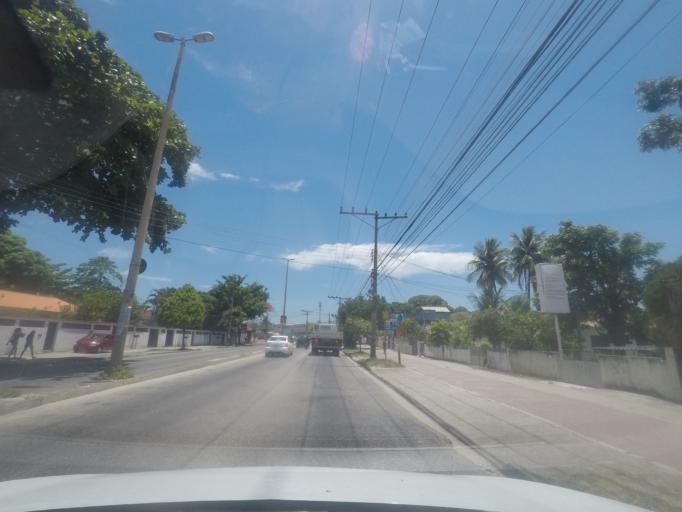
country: BR
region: Rio de Janeiro
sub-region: Itaguai
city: Itaguai
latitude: -22.9095
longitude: -43.6869
